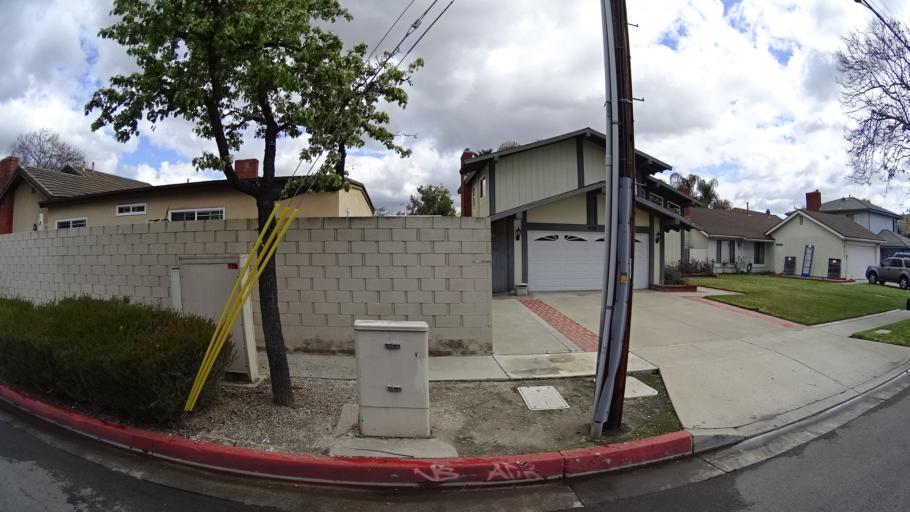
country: US
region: California
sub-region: Orange County
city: Anaheim
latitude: 33.8271
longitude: -117.9371
